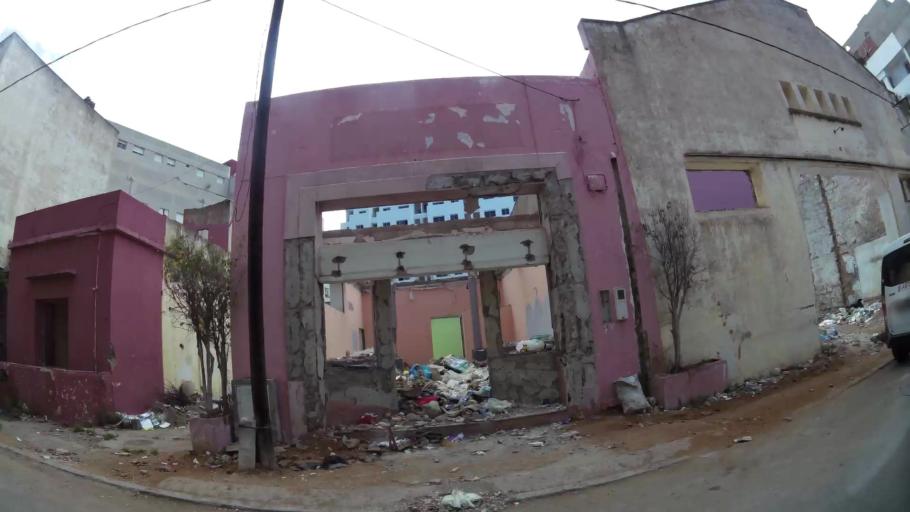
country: MA
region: Gharb-Chrarda-Beni Hssen
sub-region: Kenitra Province
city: Kenitra
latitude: 34.2576
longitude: -6.5871
